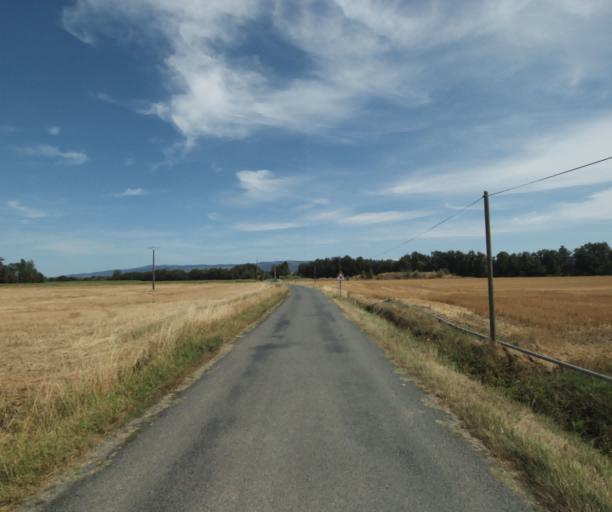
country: FR
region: Midi-Pyrenees
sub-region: Departement du Tarn
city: Puylaurens
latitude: 43.5172
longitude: 2.0180
